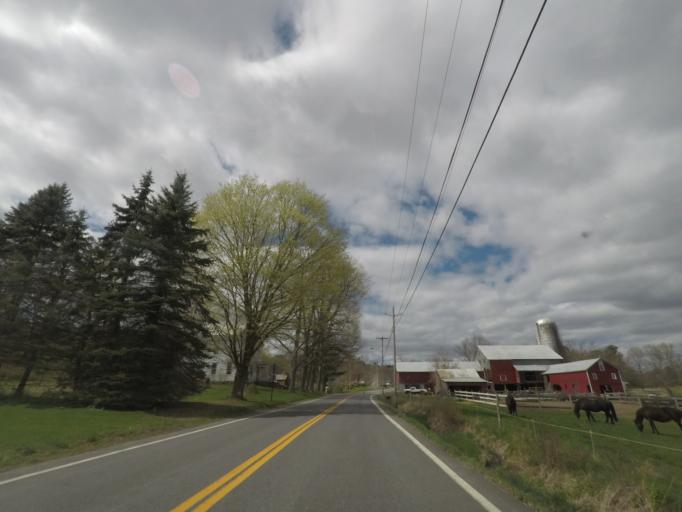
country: US
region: New York
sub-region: Columbia County
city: Philmont
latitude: 42.2591
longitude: -73.6649
